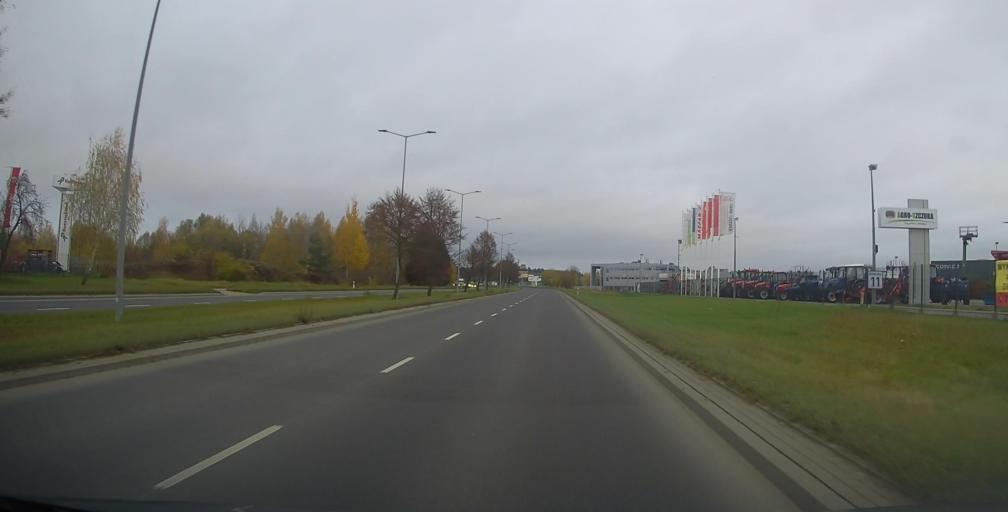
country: PL
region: Warmian-Masurian Voivodeship
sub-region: Powiat elcki
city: Elk
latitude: 53.8270
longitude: 22.3916
